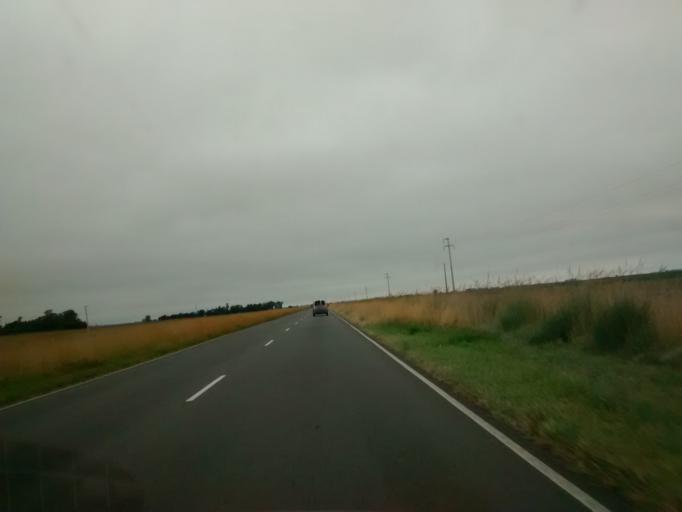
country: AR
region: Buenos Aires
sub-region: Partido de Ayacucho
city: Ayacucho
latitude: -37.0415
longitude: -58.5410
